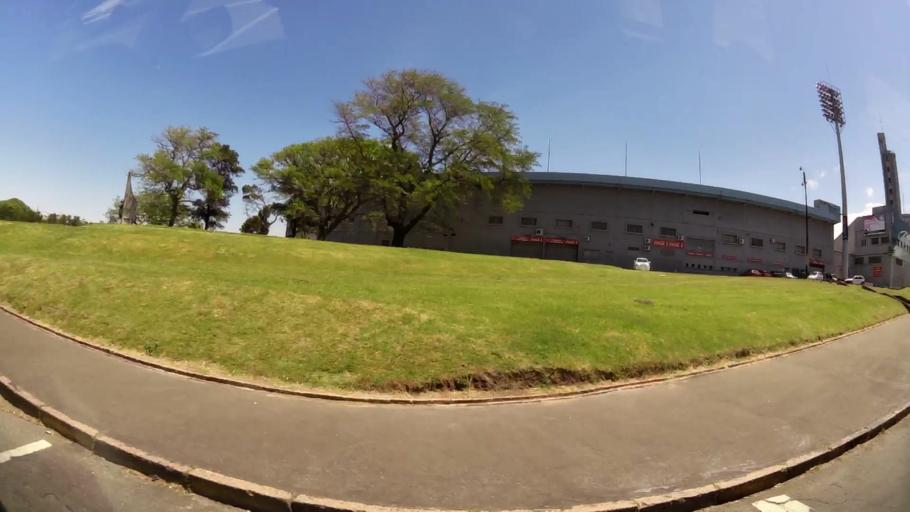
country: UY
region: Montevideo
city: Montevideo
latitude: -34.8957
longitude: -56.1511
